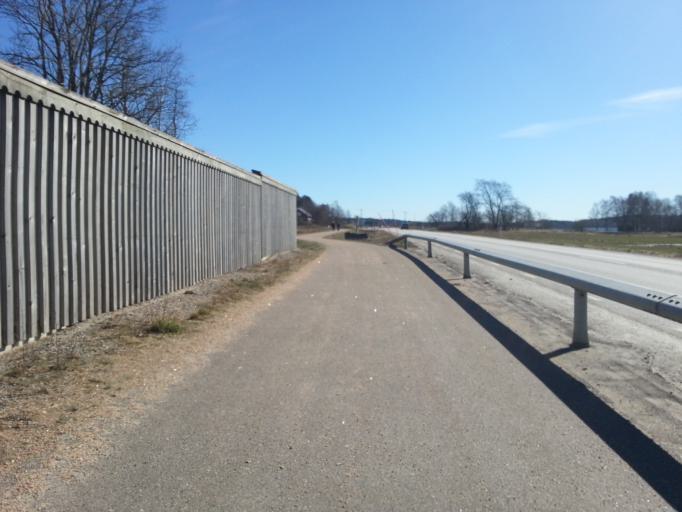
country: SE
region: Vaestra Goetaland
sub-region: Kungalvs Kommun
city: Kungalv
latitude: 57.9037
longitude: 11.9262
